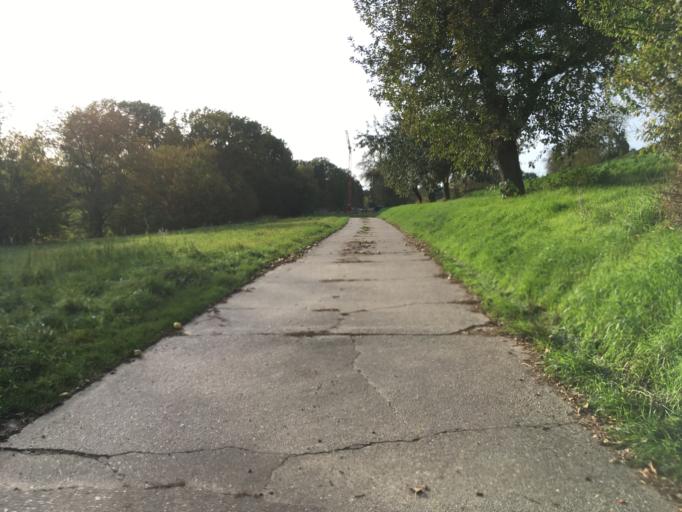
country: DE
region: Baden-Wuerttemberg
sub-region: Karlsruhe Region
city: Zuzenhausen
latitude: 49.2705
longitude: 8.8301
